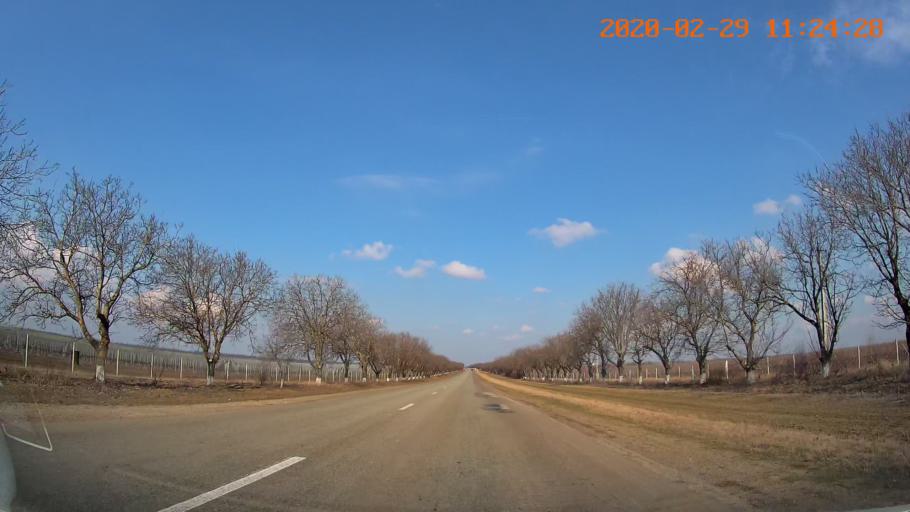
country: MD
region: Telenesti
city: Cocieri
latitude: 47.4241
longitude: 29.1545
